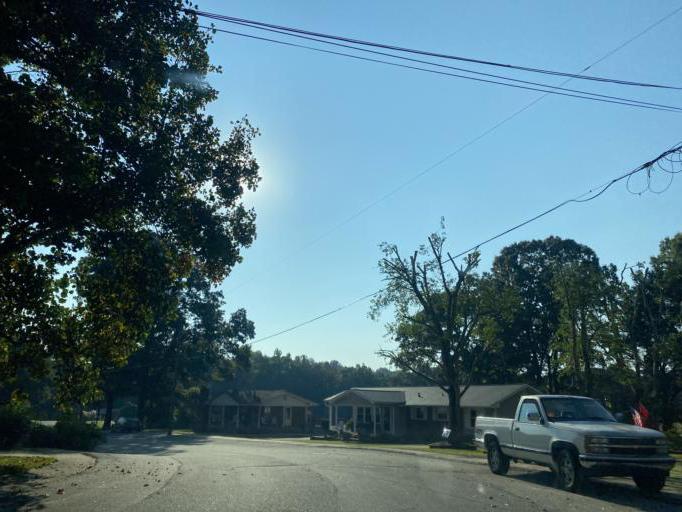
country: US
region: South Carolina
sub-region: Cherokee County
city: Gaffney
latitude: 35.0551
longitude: -81.6623
